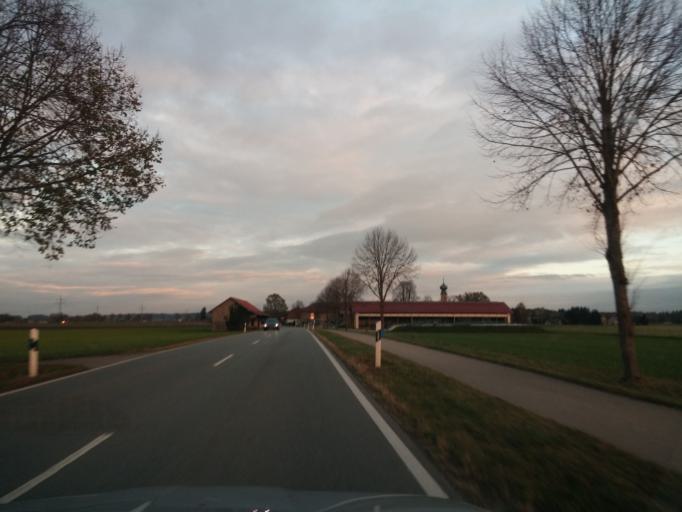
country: DE
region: Bavaria
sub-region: Upper Bavaria
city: Forstinning
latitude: 48.1692
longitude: 11.9351
